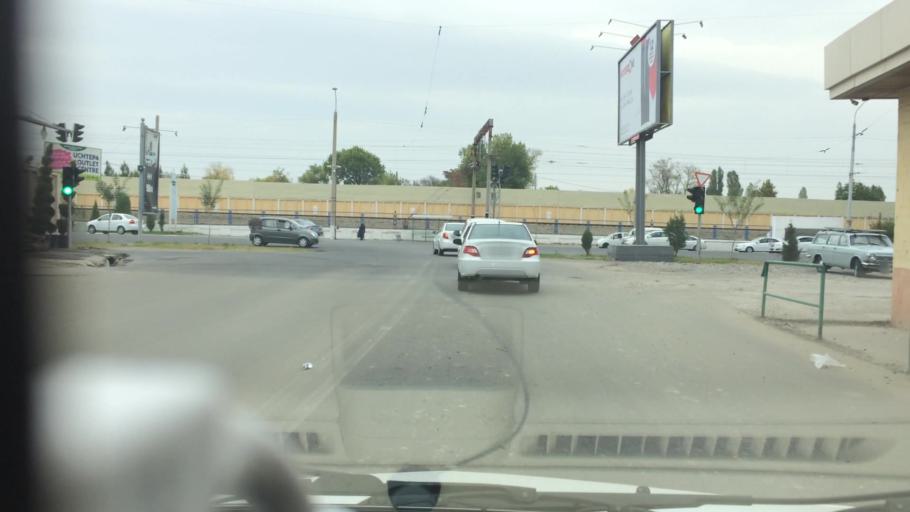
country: UZ
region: Toshkent Shahri
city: Tashkent
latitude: 41.2784
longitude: 69.2721
